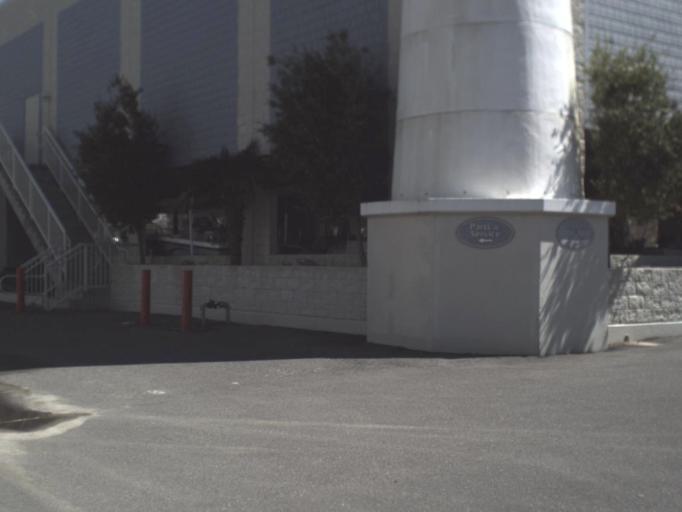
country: US
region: Florida
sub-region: Leon County
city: Woodville
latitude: 30.1550
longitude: -84.2024
